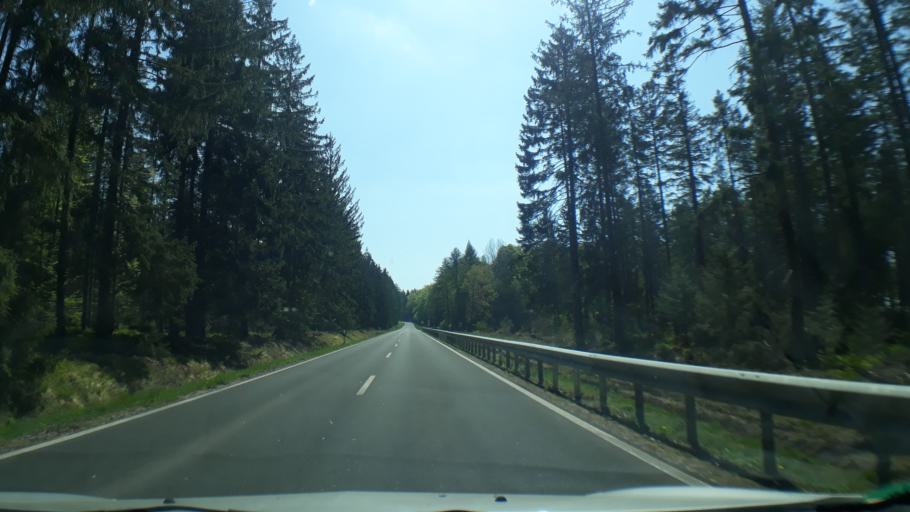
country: DE
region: North Rhine-Westphalia
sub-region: Regierungsbezirk Koln
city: Roetgen
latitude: 50.6653
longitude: 6.2467
